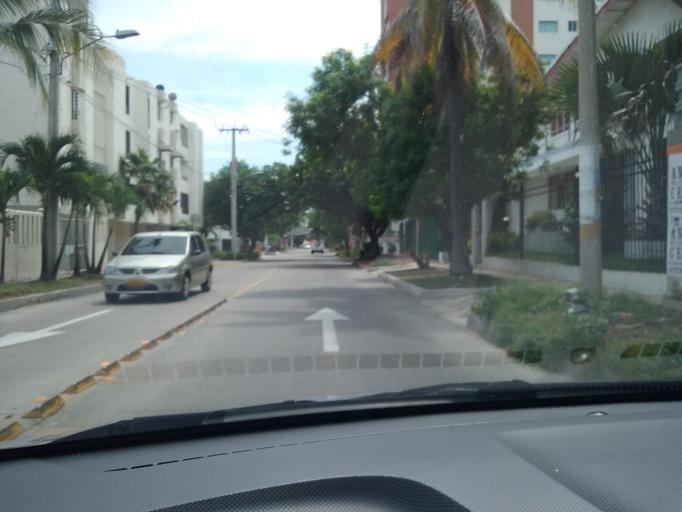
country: CO
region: Atlantico
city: Barranquilla
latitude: 11.0113
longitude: -74.8072
